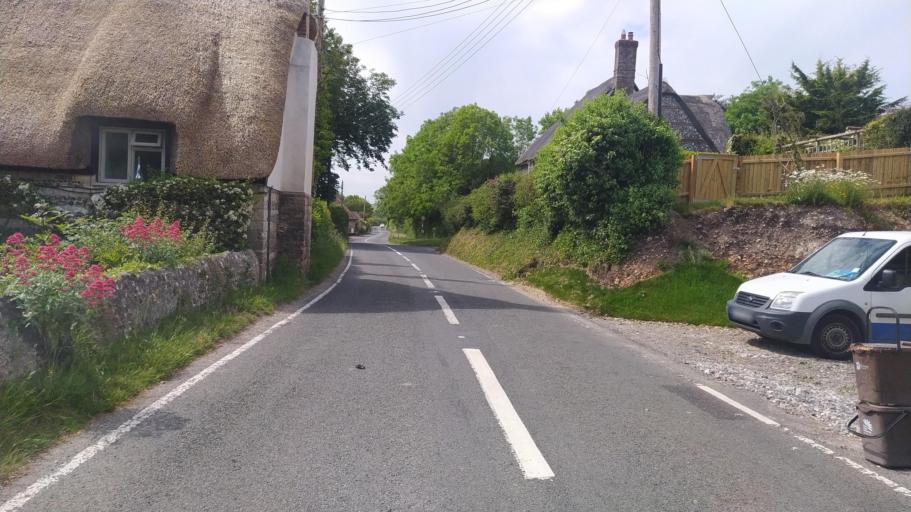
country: GB
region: England
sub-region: Dorset
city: Dorchester
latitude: 50.7719
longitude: -2.4749
